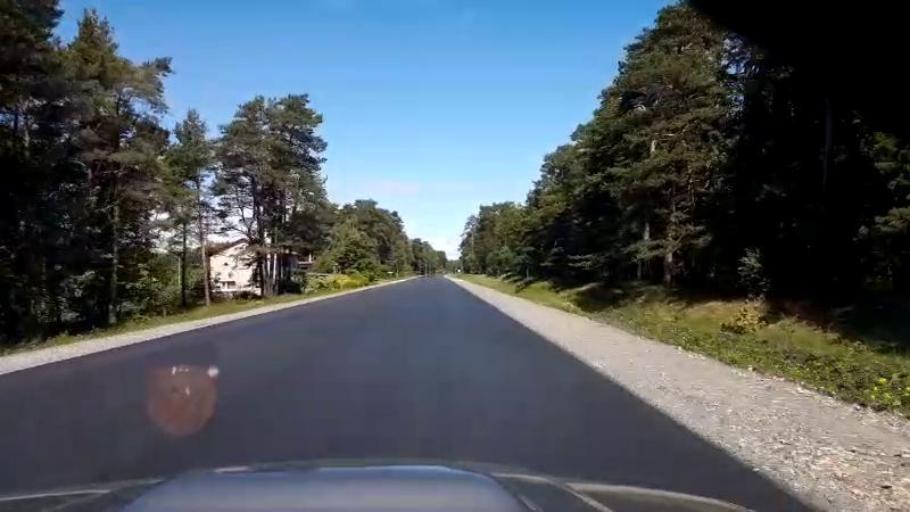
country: LV
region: Salacgrivas
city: Ainazi
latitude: 57.8132
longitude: 24.3474
